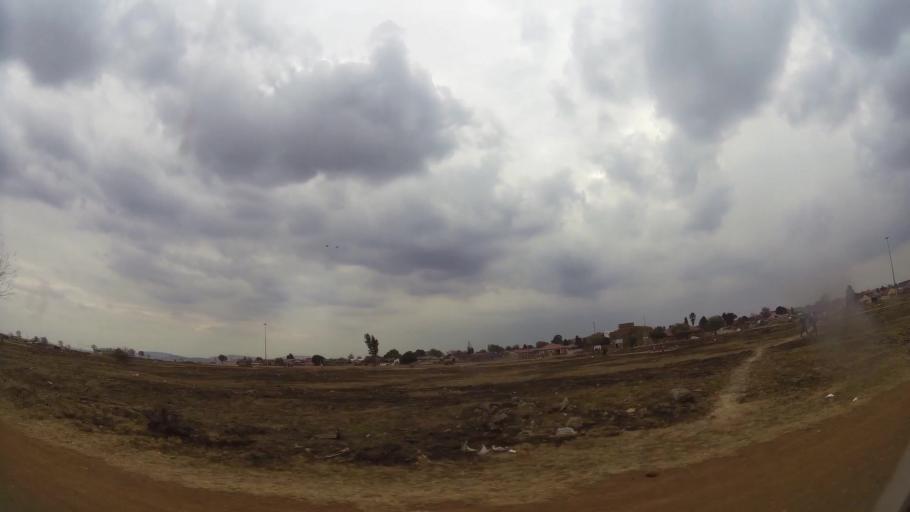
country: ZA
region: Gauteng
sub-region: Ekurhuleni Metropolitan Municipality
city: Germiston
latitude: -26.3839
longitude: 28.1363
